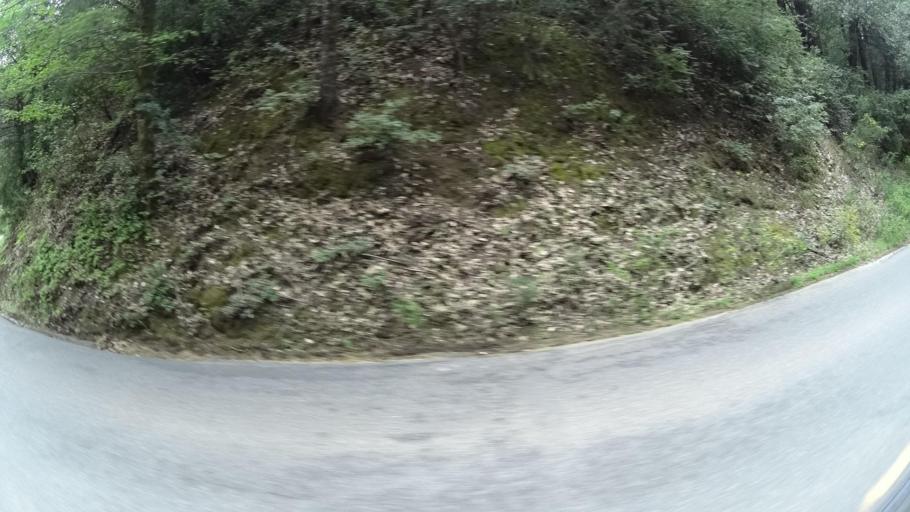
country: US
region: California
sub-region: Humboldt County
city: Redway
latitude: 40.1040
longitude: -123.9180
